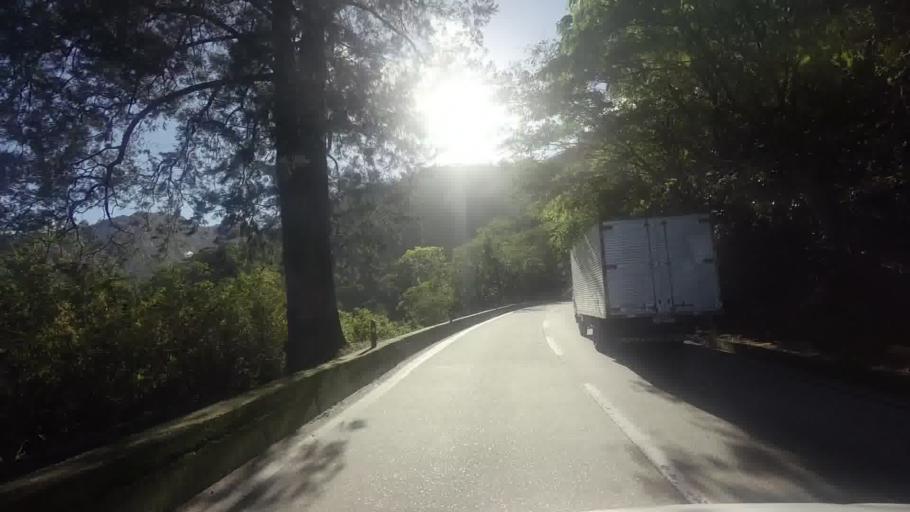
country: BR
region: Rio de Janeiro
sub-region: Petropolis
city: Petropolis
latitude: -22.5648
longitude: -43.2383
